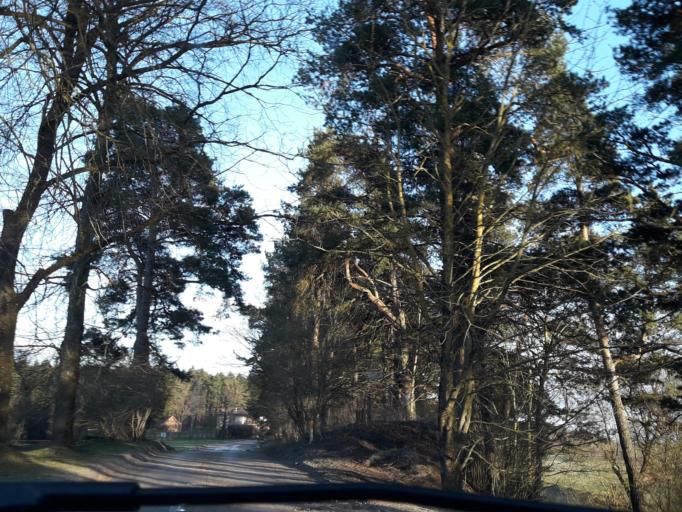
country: LV
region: Kekava
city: Kekava
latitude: 56.8615
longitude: 24.2168
